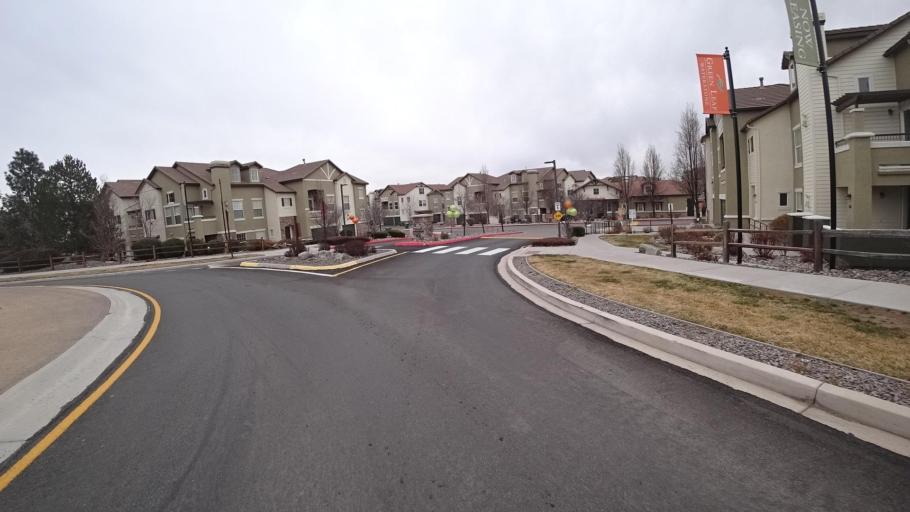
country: US
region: Nevada
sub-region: Washoe County
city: Sun Valley
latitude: 39.6031
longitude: -119.7317
